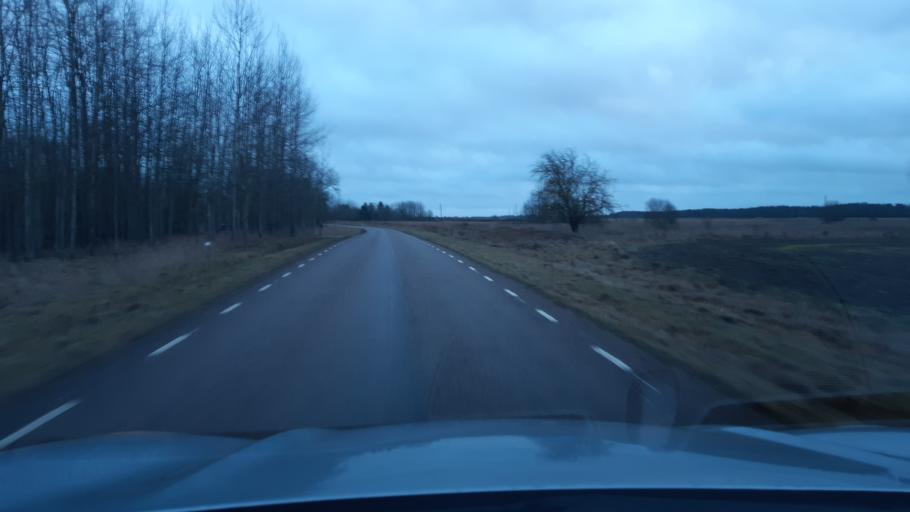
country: EE
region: Raplamaa
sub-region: Rapla vald
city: Rapla
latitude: 59.0046
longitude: 24.7129
